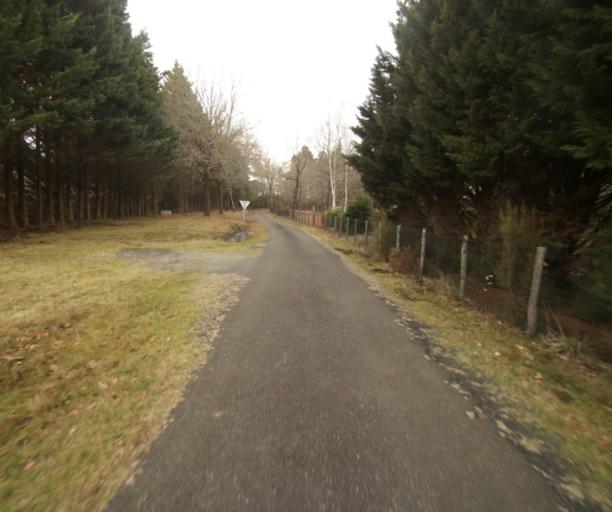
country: FR
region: Aquitaine
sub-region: Departement des Landes
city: Gabarret
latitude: 44.1004
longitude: -0.0171
